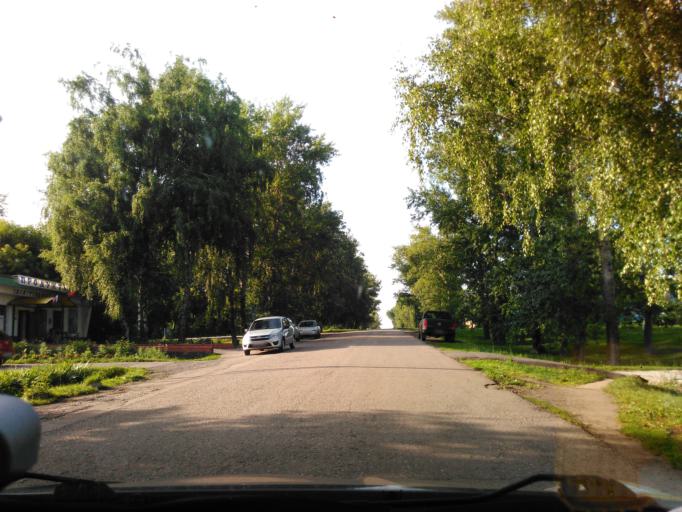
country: RU
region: Penza
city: Lermontovo
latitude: 52.9934
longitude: 43.6584
